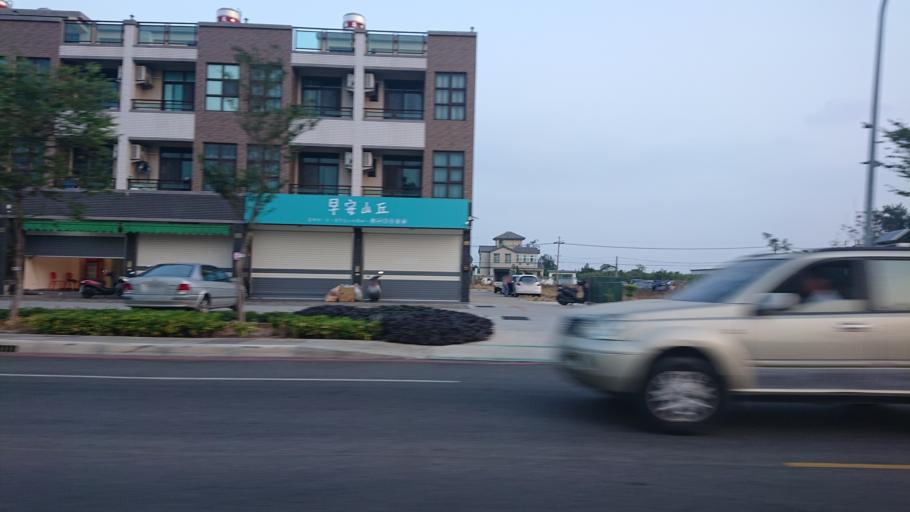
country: TW
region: Fukien
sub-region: Kinmen
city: Jincheng
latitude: 24.4431
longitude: 118.3247
